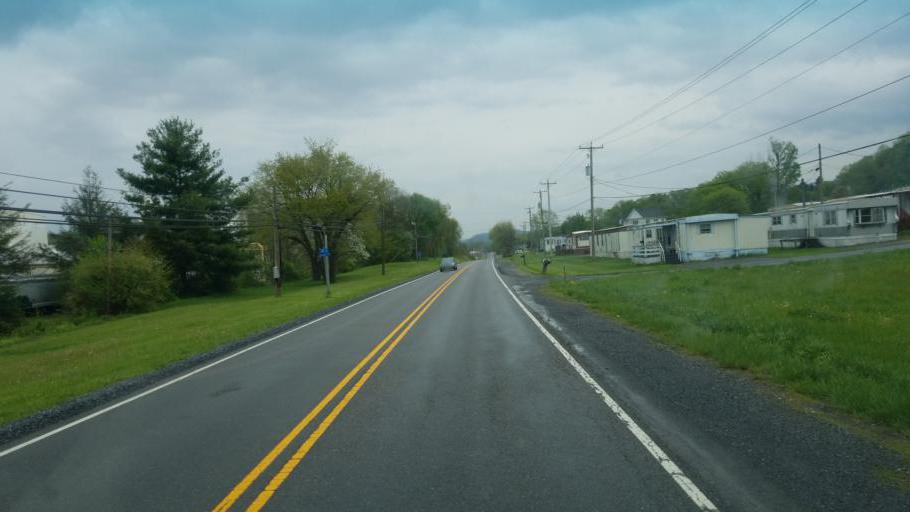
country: US
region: Virginia
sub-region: Smyth County
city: Atkins
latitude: 36.8628
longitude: -81.4472
